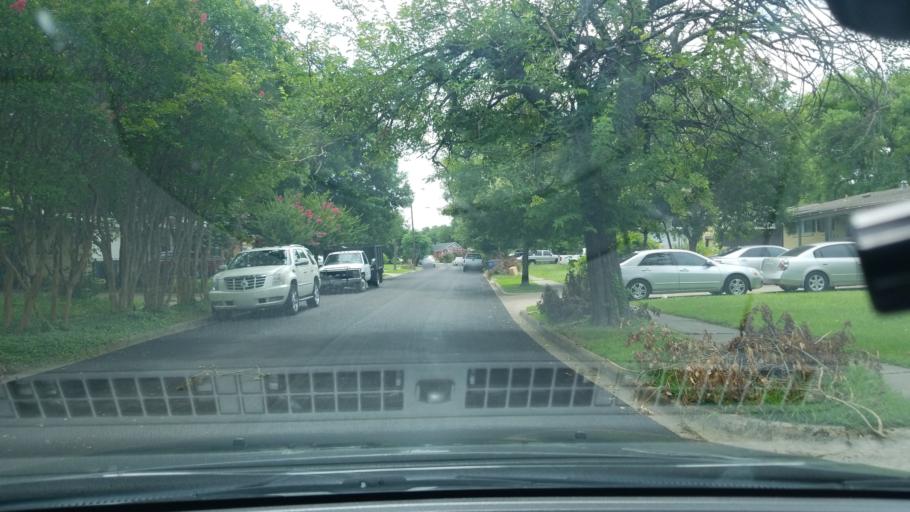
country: US
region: Texas
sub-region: Dallas County
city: Mesquite
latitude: 32.8183
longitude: -96.6762
